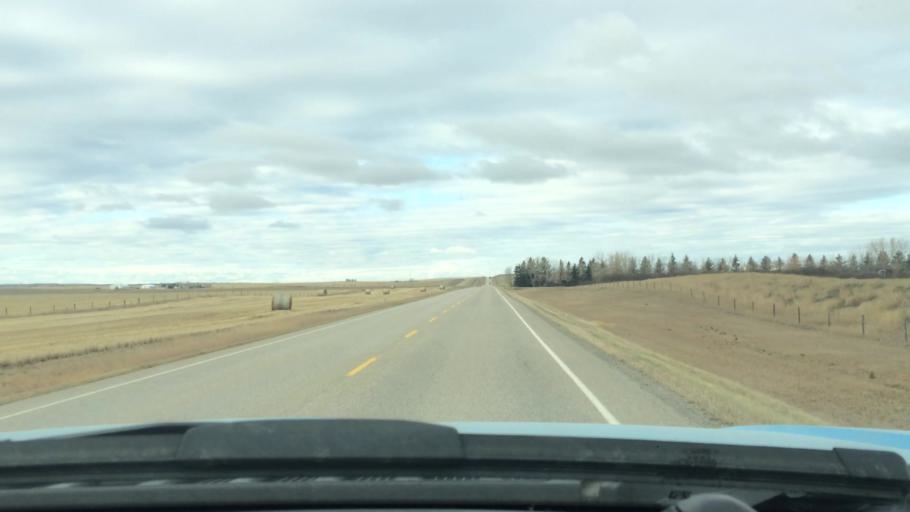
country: CA
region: Alberta
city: Airdrie
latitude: 51.2125
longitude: -114.0862
